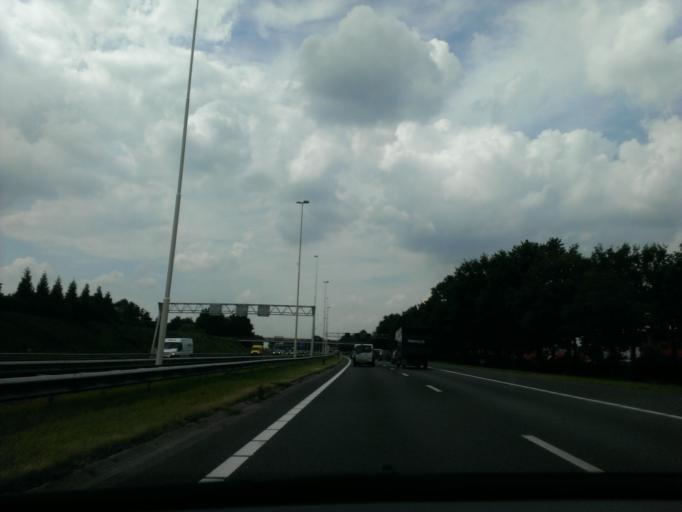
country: NL
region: Utrecht
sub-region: Gemeente Amersfoort
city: Hoogland
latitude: 52.2019
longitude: 5.3918
